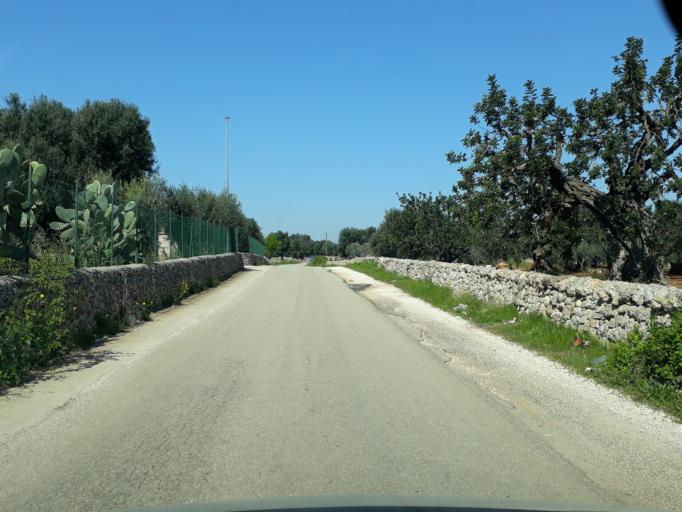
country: IT
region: Apulia
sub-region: Provincia di Brindisi
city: Fasano
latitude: 40.8294
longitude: 17.3804
